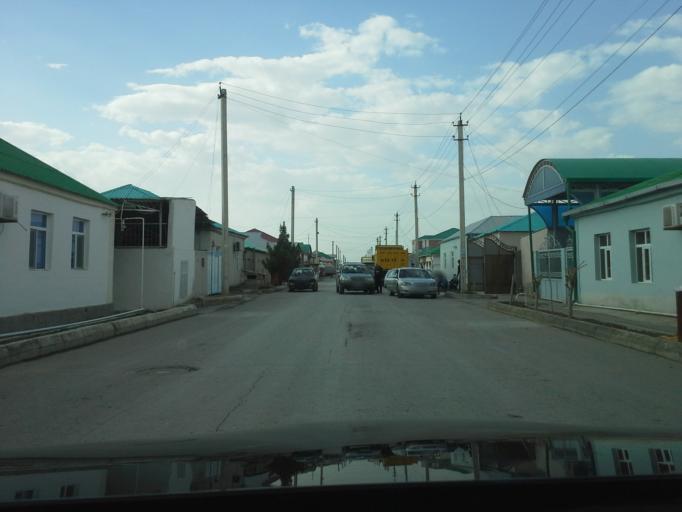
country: TM
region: Ahal
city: Ashgabat
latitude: 37.9898
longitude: 58.2950
